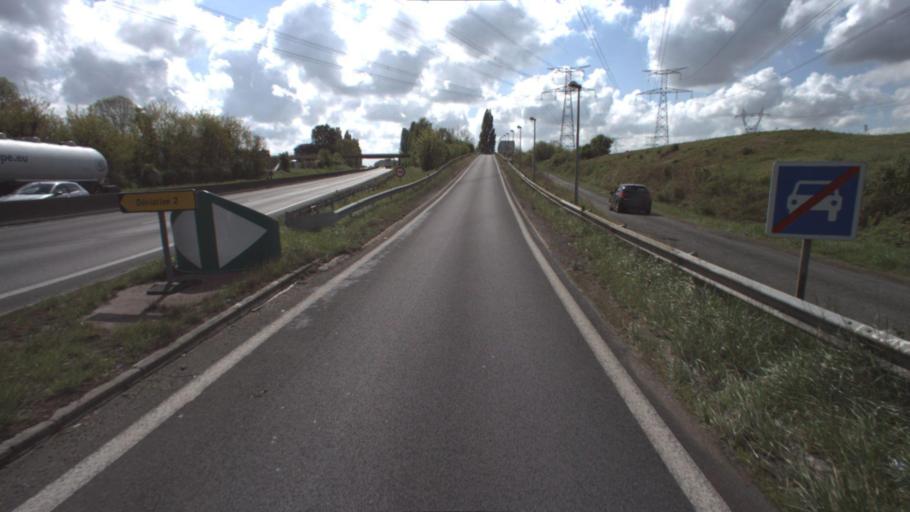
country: FR
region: Ile-de-France
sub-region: Departement de Seine-et-Marne
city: Ozoir-la-Ferriere
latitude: 48.7629
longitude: 2.6604
